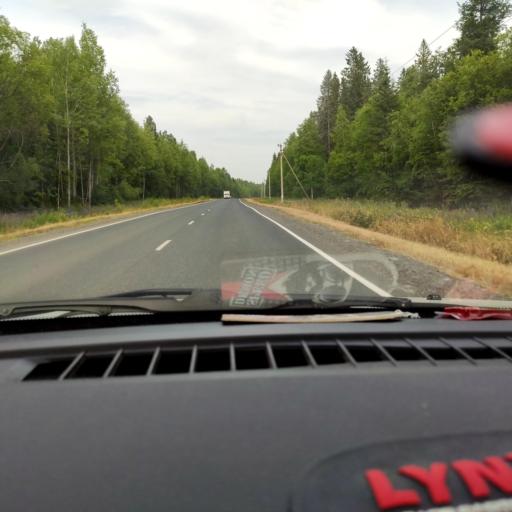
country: RU
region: Perm
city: Perm
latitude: 58.1950
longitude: 56.2565
